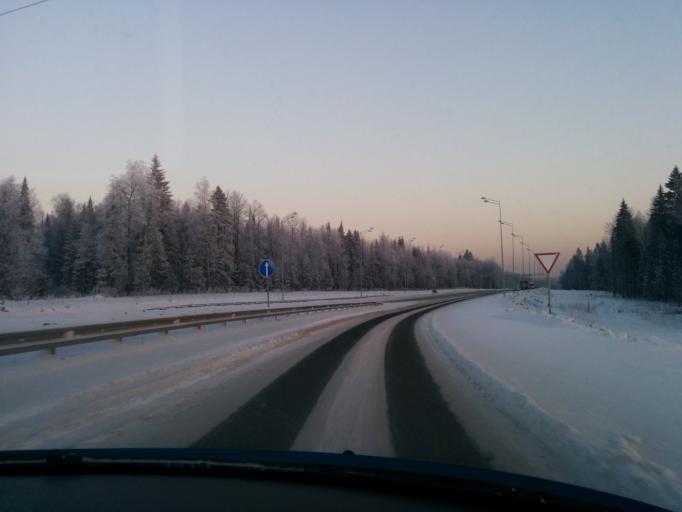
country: RU
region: Perm
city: Novyye Lyady
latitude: 58.0441
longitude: 56.4370
